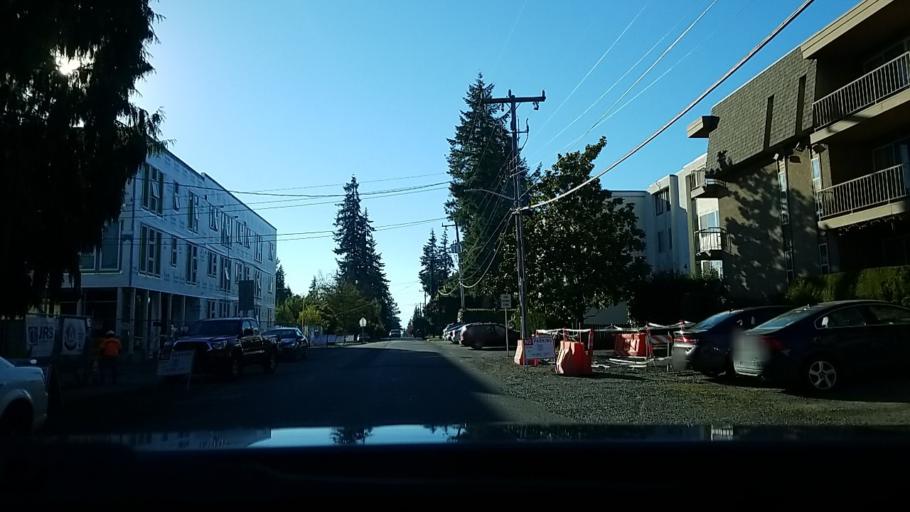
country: US
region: Washington
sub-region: King County
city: Shoreline
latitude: 47.7251
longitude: -122.3559
